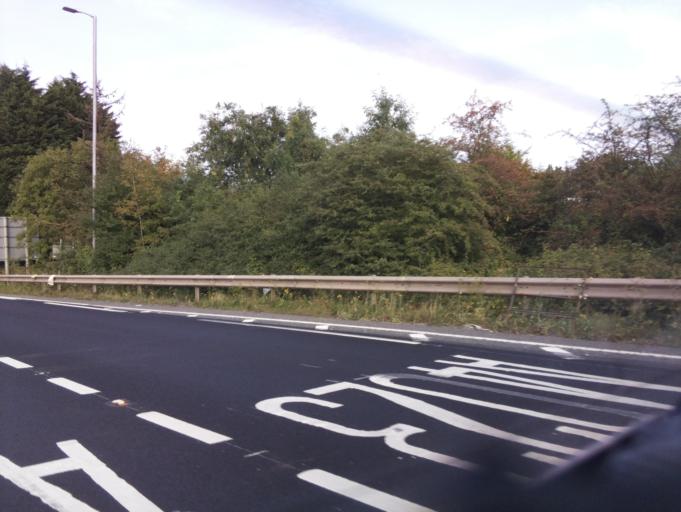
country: GB
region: England
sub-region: Warwickshire
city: Studley
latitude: 52.3099
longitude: -1.8726
